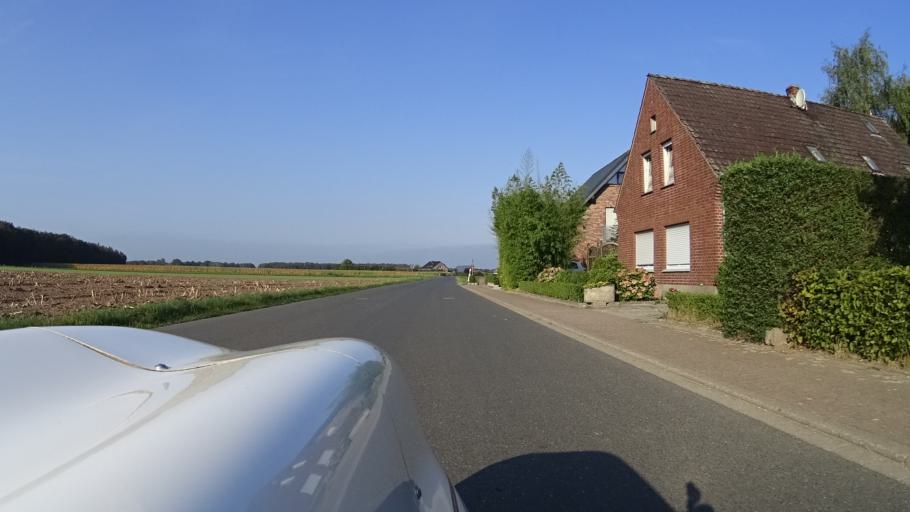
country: DE
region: North Rhine-Westphalia
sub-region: Regierungsbezirk Dusseldorf
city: Kevelaer
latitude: 51.5510
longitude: 6.1974
